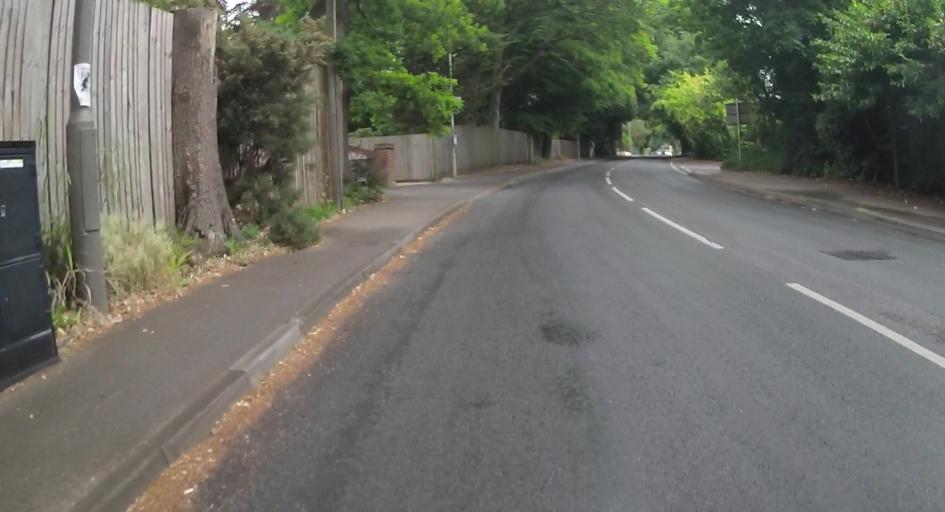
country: GB
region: England
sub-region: Hampshire
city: Fleet
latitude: 51.2627
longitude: -0.8485
